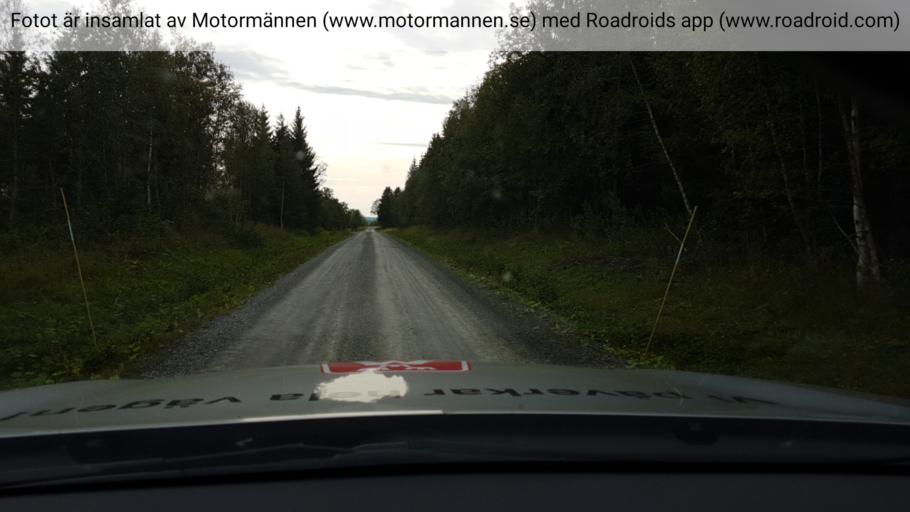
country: SE
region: Jaemtland
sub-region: Krokoms Kommun
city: Valla
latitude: 63.5741
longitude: 13.9356
